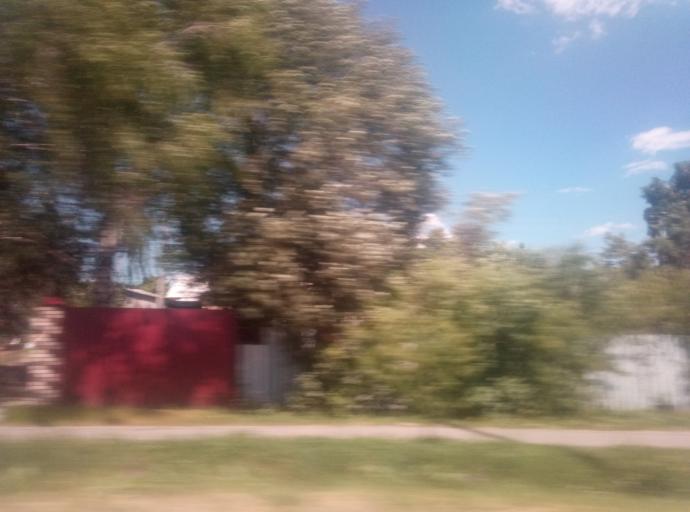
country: RU
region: Tula
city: Kireyevsk
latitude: 54.0161
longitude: 37.9170
